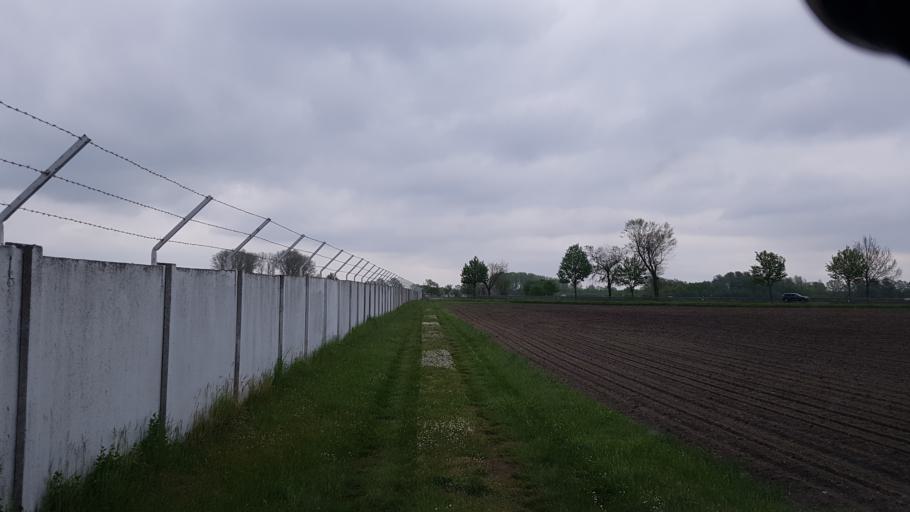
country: DE
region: Brandenburg
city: Doberlug-Kirchhain
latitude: 51.6044
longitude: 13.5349
